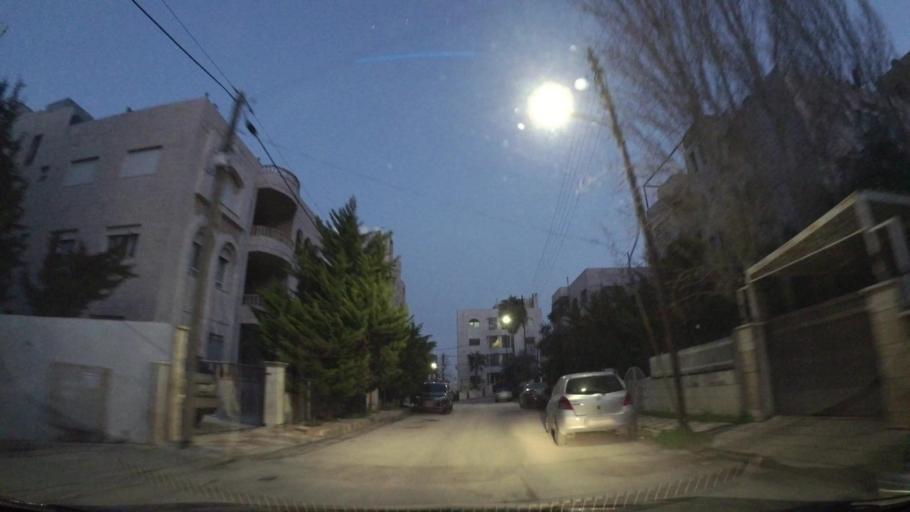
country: JO
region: Amman
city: Al Jubayhah
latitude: 31.9842
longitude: 35.8843
